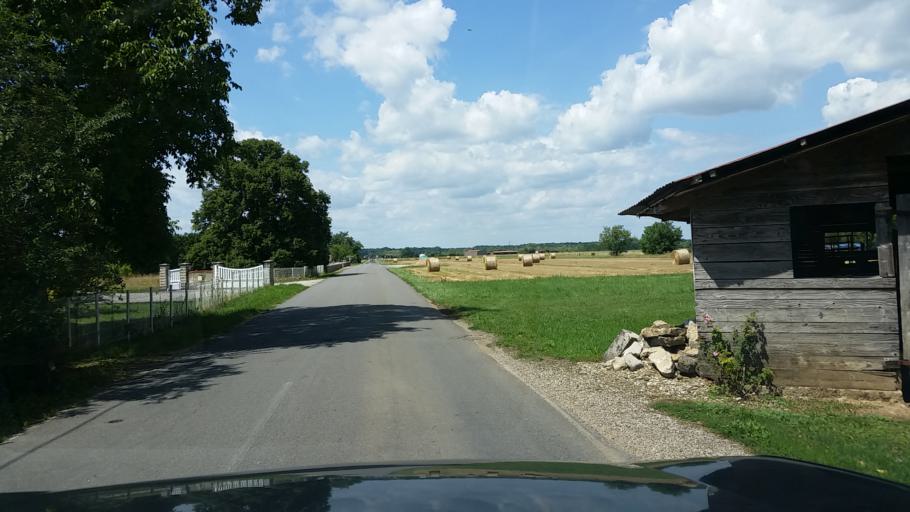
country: FR
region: Franche-Comte
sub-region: Departement du Jura
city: Bletterans
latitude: 46.7463
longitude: 5.4922
